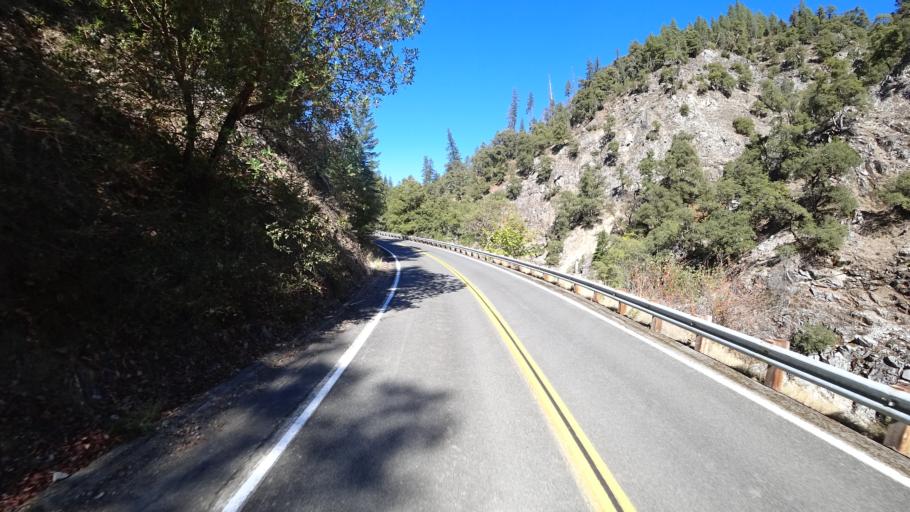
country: US
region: California
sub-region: Siskiyou County
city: Happy Camp
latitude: 41.3499
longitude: -123.4070
